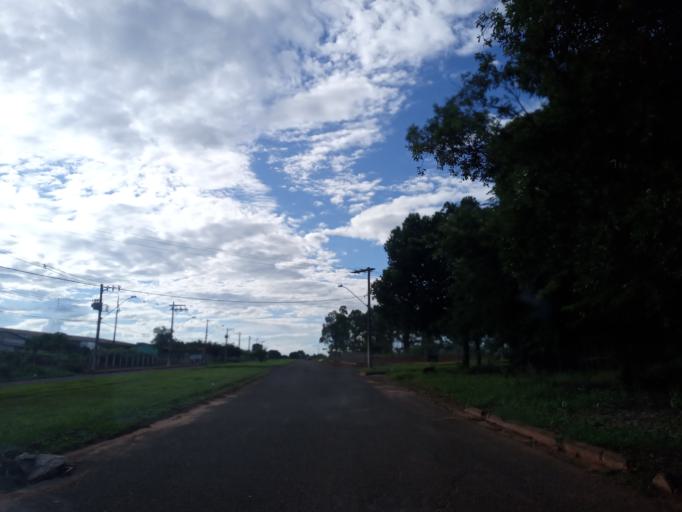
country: BR
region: Minas Gerais
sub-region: Ituiutaba
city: Ituiutaba
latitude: -18.9632
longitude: -49.4906
